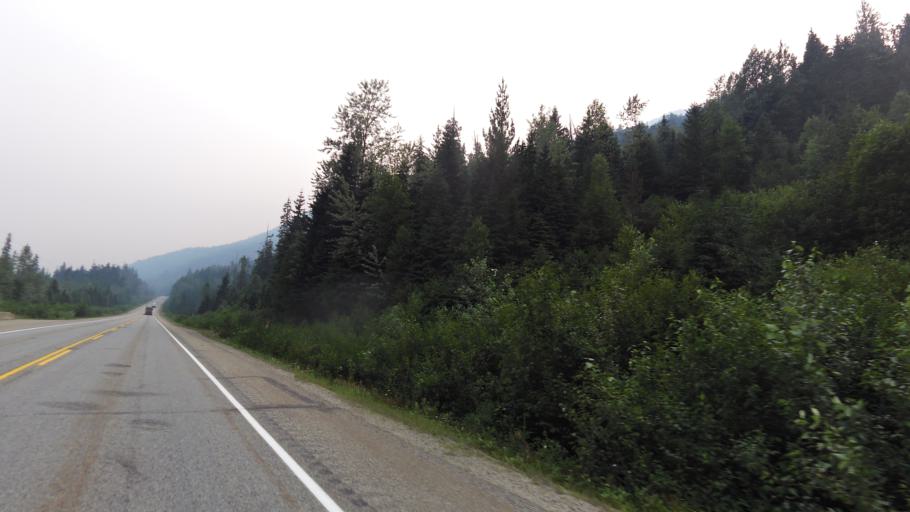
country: CA
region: Alberta
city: Jasper Park Lodge
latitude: 52.3166
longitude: -119.1781
